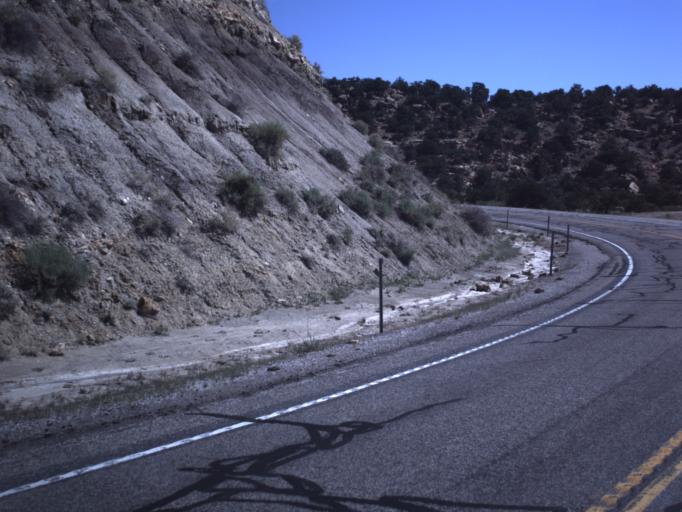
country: US
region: Utah
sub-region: Wayne County
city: Loa
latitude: 38.6718
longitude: -111.4060
